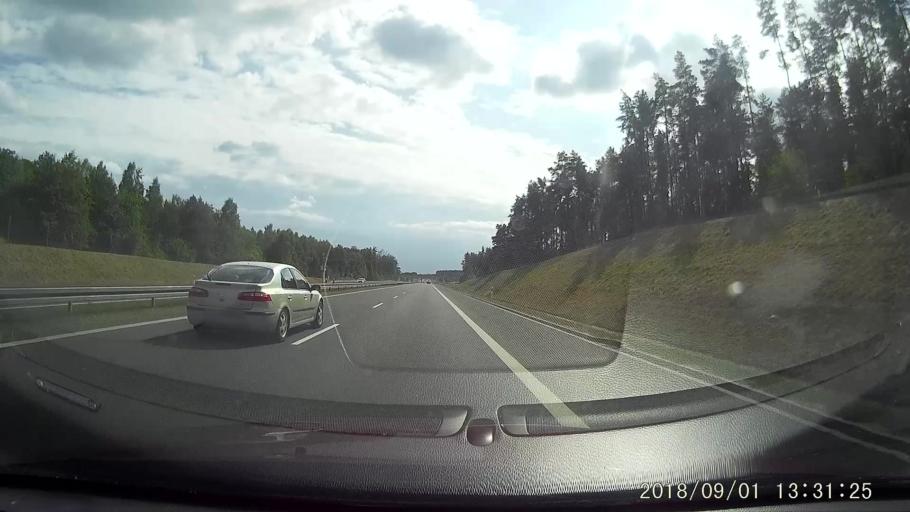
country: PL
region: West Pomeranian Voivodeship
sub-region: Powiat mysliborski
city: Mysliborz
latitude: 53.0178
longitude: 14.8614
